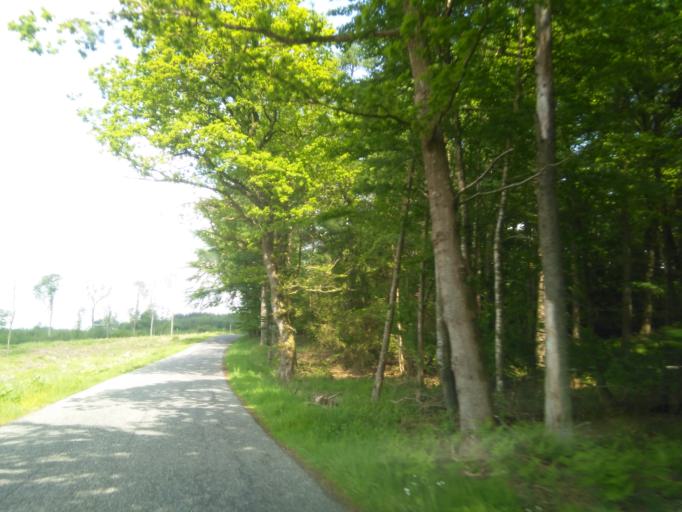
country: DK
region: Central Jutland
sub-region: Skanderborg Kommune
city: Galten
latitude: 56.2230
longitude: 9.9280
